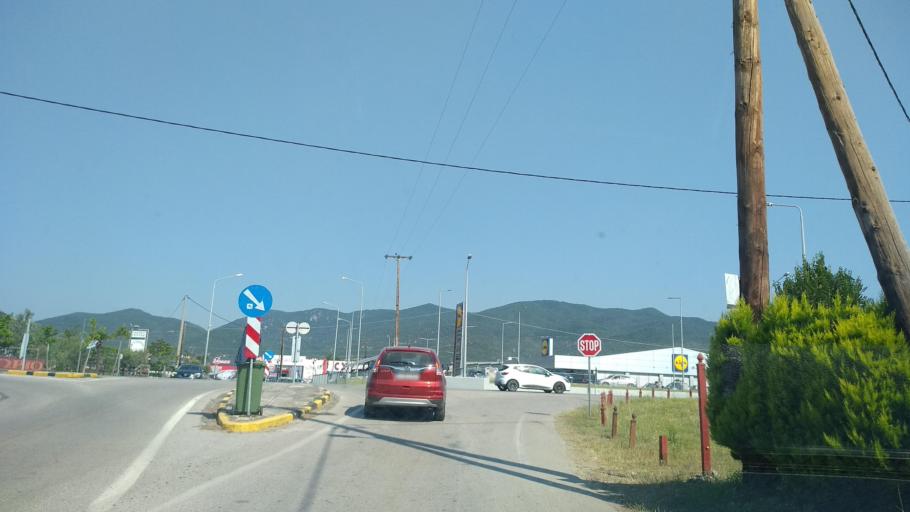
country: GR
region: Central Macedonia
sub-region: Nomos Thessalonikis
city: Nea Vrasna
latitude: 40.6919
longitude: 23.6838
